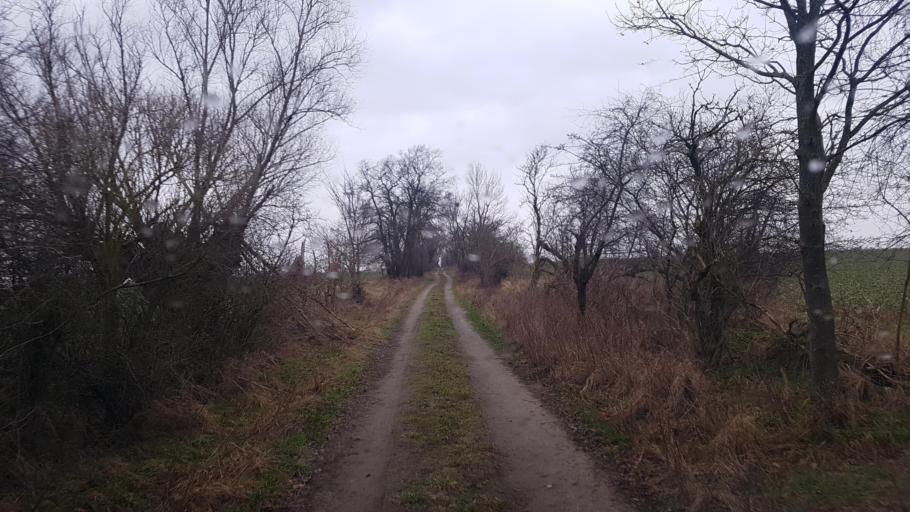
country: DE
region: Brandenburg
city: Zehdenick
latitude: 52.9486
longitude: 13.2558
